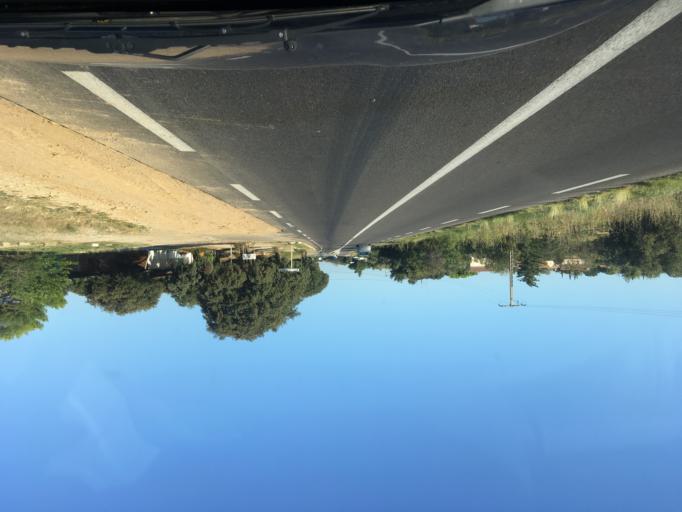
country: FR
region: Languedoc-Roussillon
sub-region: Departement du Gard
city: Ledenon
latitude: 43.9074
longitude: 4.5220
